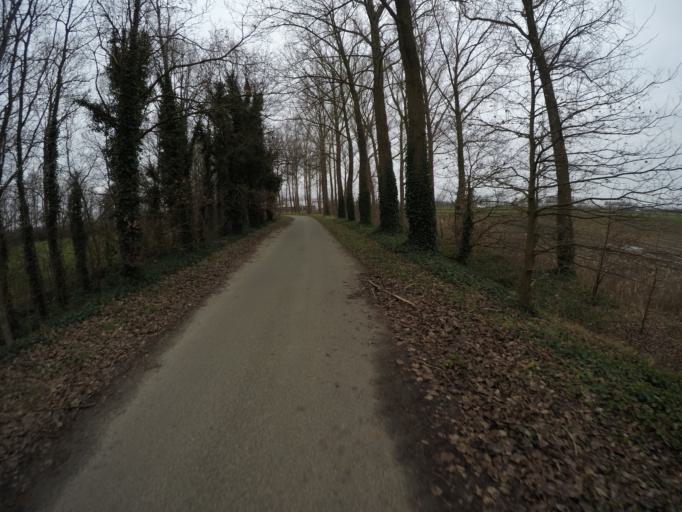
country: BE
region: Flanders
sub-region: Provincie Oost-Vlaanderen
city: Sint-Gillis-Waas
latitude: 51.2335
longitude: 4.1299
